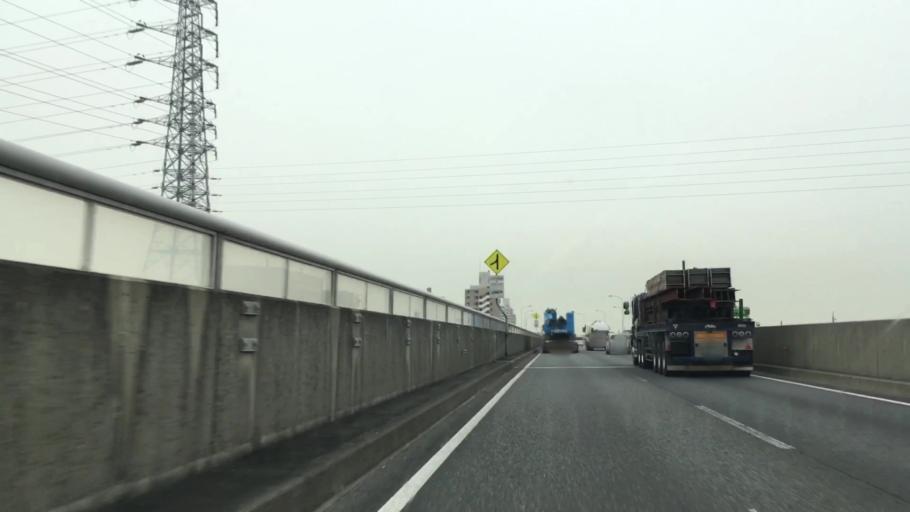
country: JP
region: Aichi
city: Chiryu
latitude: 34.9774
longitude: 137.0363
